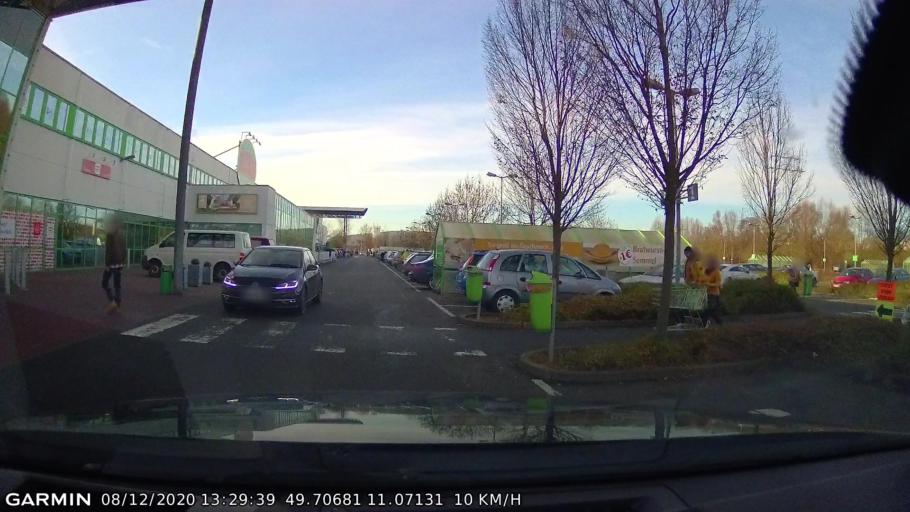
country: DE
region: Bavaria
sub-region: Upper Franconia
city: Forchheim
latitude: 49.7068
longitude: 11.0713
